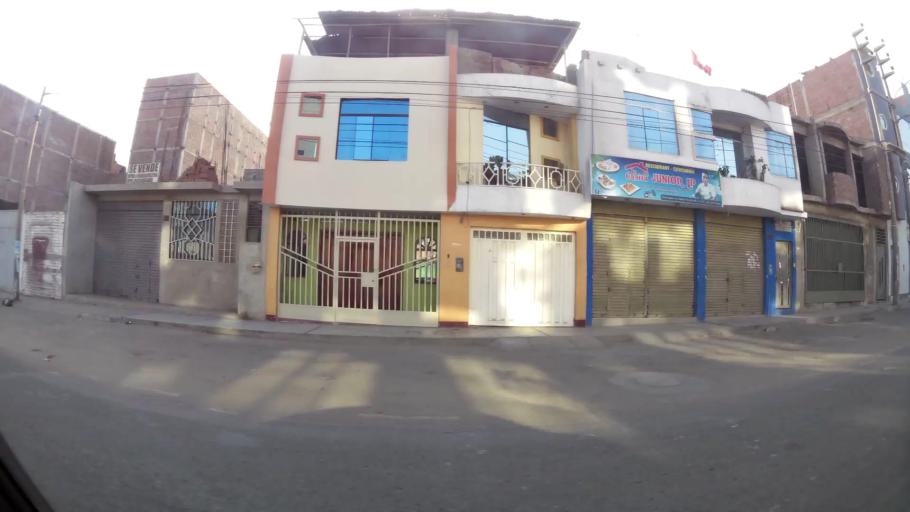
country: PE
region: La Libertad
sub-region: Provincia de Trujillo
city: El Porvenir
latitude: -8.0902
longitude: -79.0032
